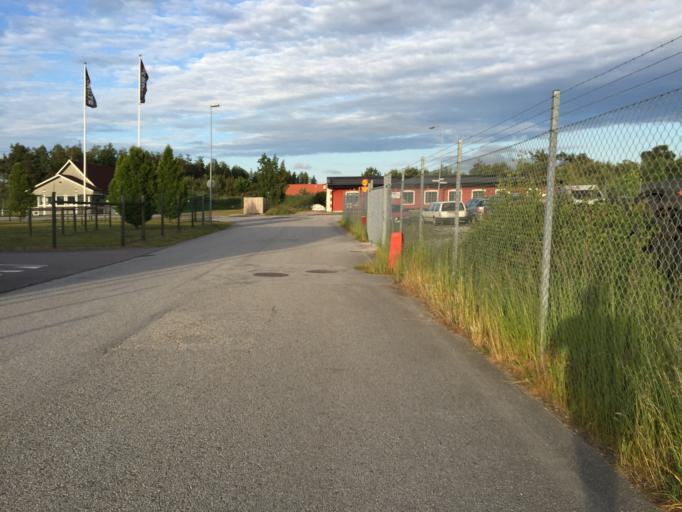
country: SE
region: Skane
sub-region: Lunds Kommun
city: Veberod
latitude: 55.6404
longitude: 13.5015
